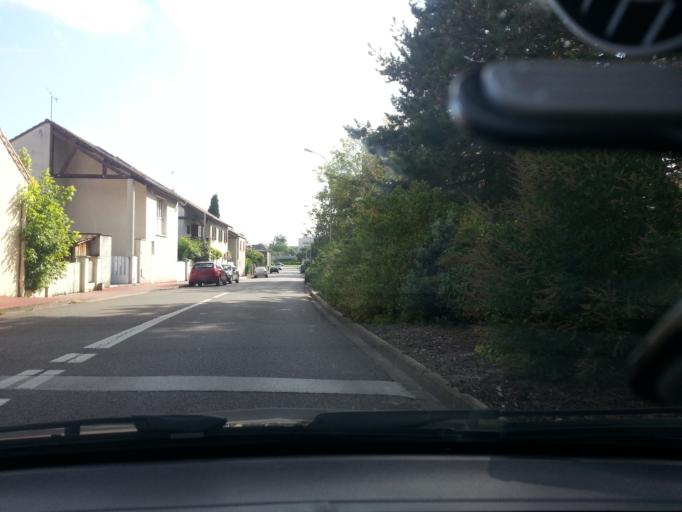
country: FR
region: Bourgogne
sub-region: Departement de Saone-et-Loire
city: Chalon-sur-Saone
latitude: 46.8023
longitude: 4.8594
